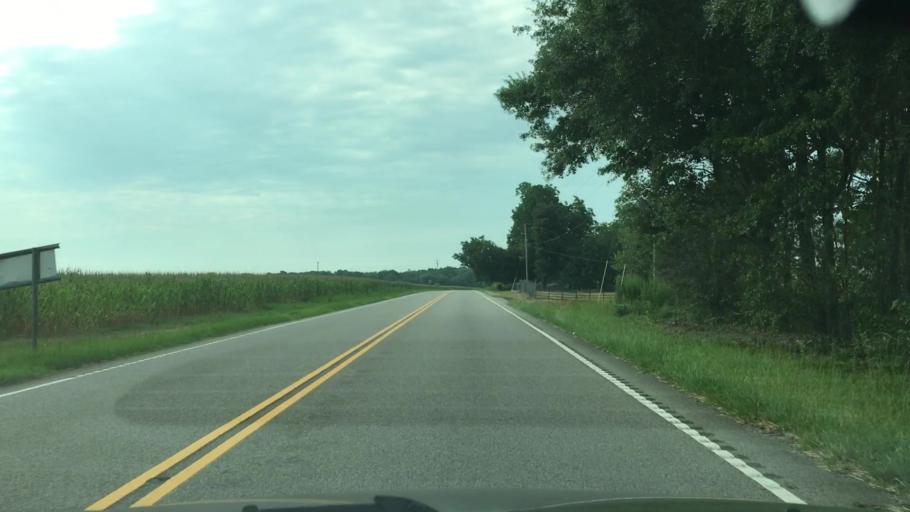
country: US
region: South Carolina
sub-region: Lexington County
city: Batesburg-Leesville
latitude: 33.7000
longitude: -81.4796
